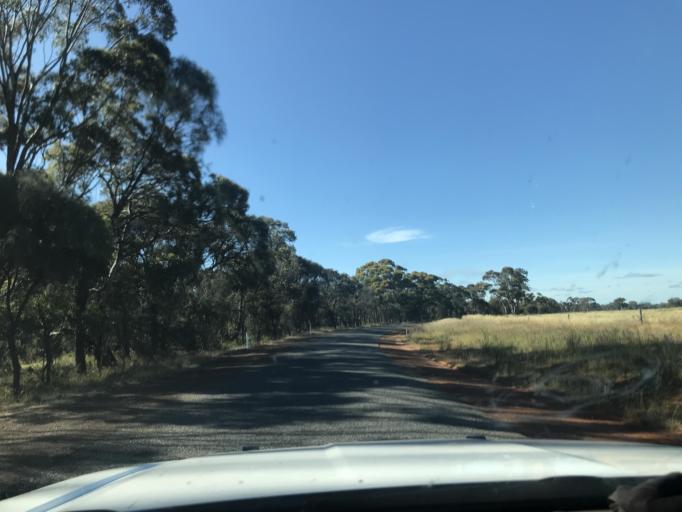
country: AU
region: Victoria
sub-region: Horsham
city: Horsham
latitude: -37.0136
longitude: 141.6734
